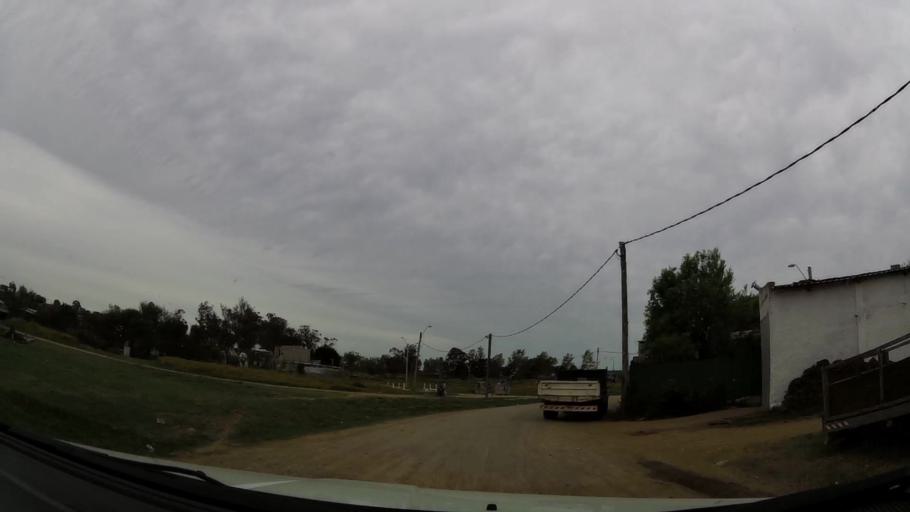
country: UY
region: Maldonado
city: Maldonado
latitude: -34.8897
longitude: -54.9573
